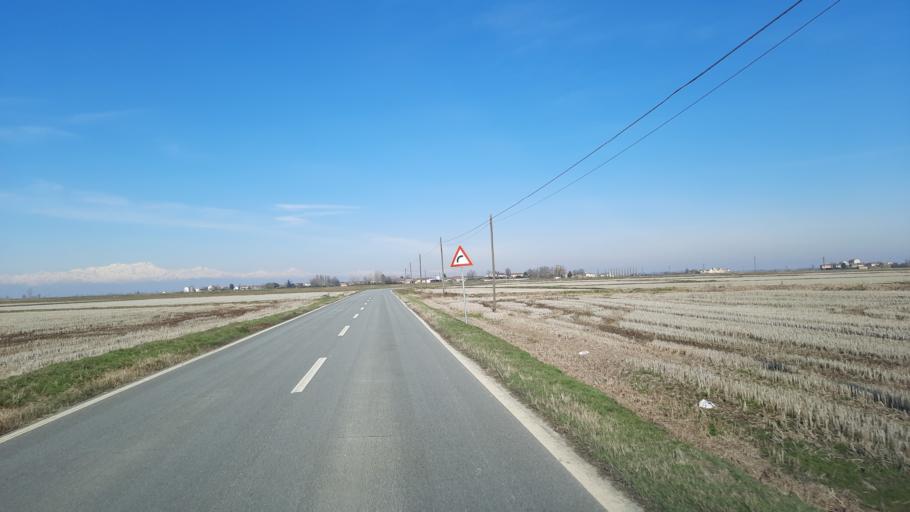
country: IT
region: Piedmont
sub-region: Provincia di Vercelli
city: Rive
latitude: 45.2241
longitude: 8.4185
